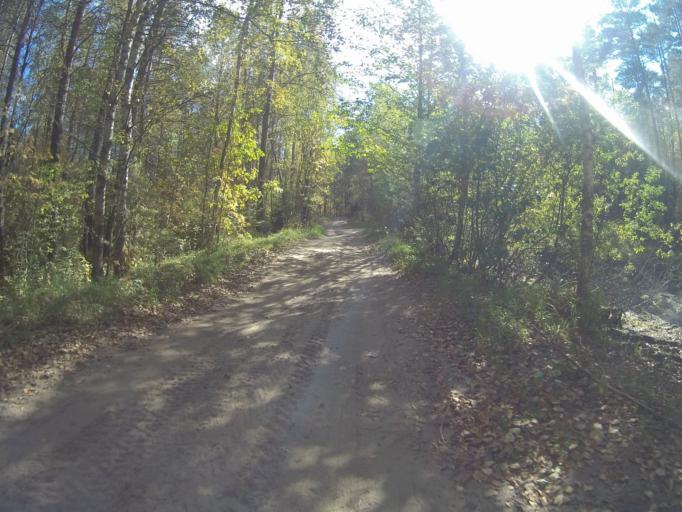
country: RU
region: Vladimir
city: Kommunar
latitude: 56.0375
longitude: 40.4640
